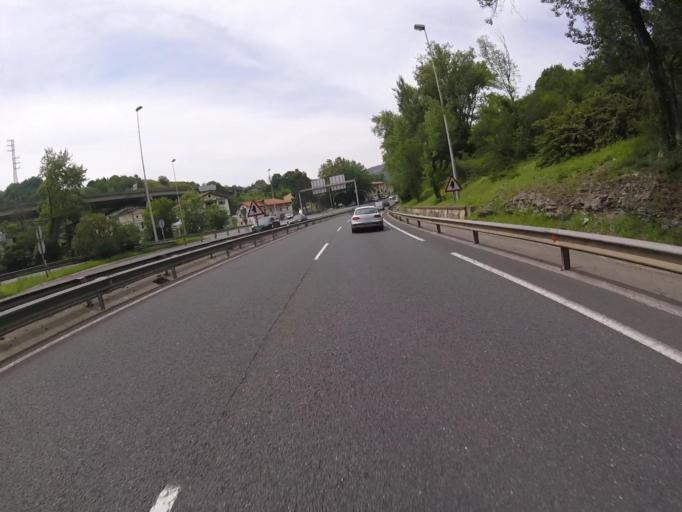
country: ES
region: Basque Country
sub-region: Provincia de Guipuzcoa
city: San Sebastian
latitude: 43.2977
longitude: -1.9988
